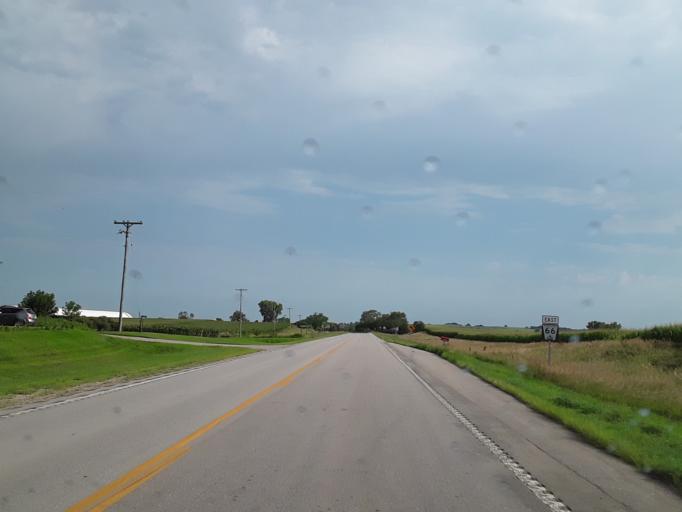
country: US
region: Nebraska
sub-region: Saunders County
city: Ashland
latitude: 41.0958
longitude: -96.4259
